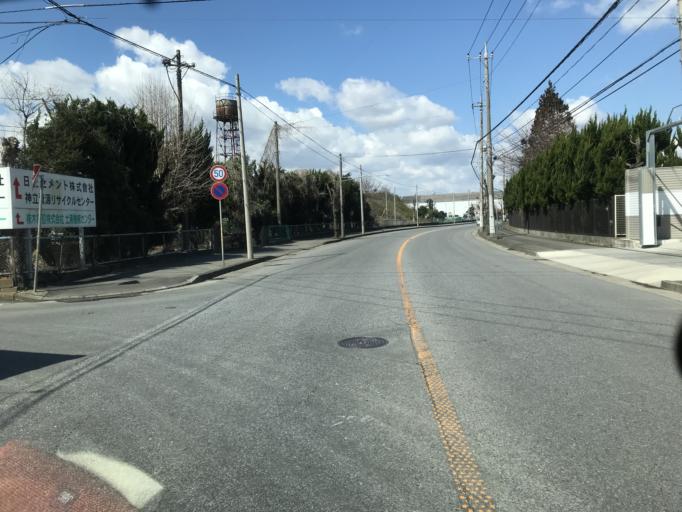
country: JP
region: Ibaraki
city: Ishioka
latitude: 36.1214
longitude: 140.2171
